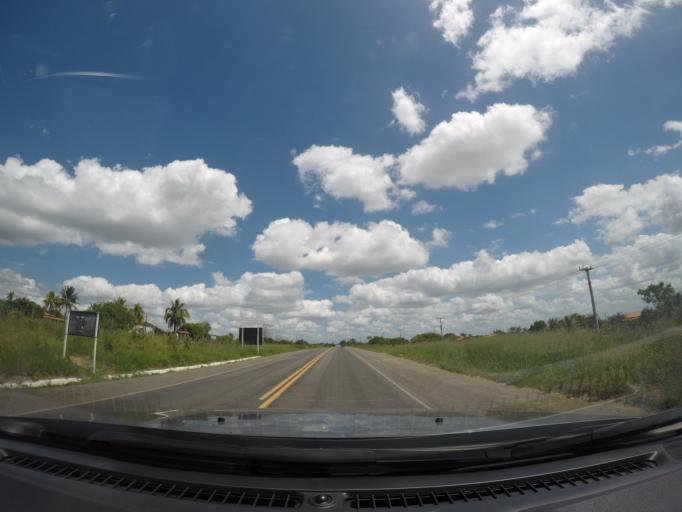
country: BR
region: Bahia
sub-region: Ipira
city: Ipira
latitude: -12.1871
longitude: -39.7047
